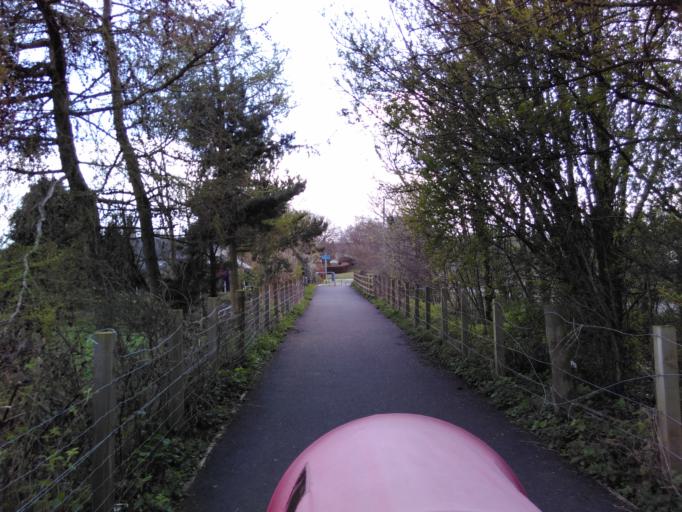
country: GB
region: Scotland
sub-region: Midlothian
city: Loanhead
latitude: 55.8640
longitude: -3.1526
